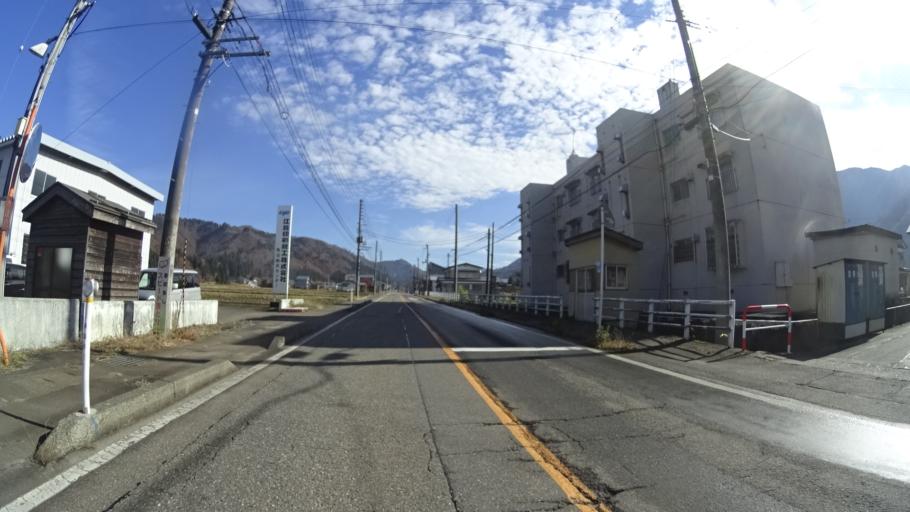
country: JP
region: Niigata
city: Muikamachi
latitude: 37.2275
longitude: 138.9968
